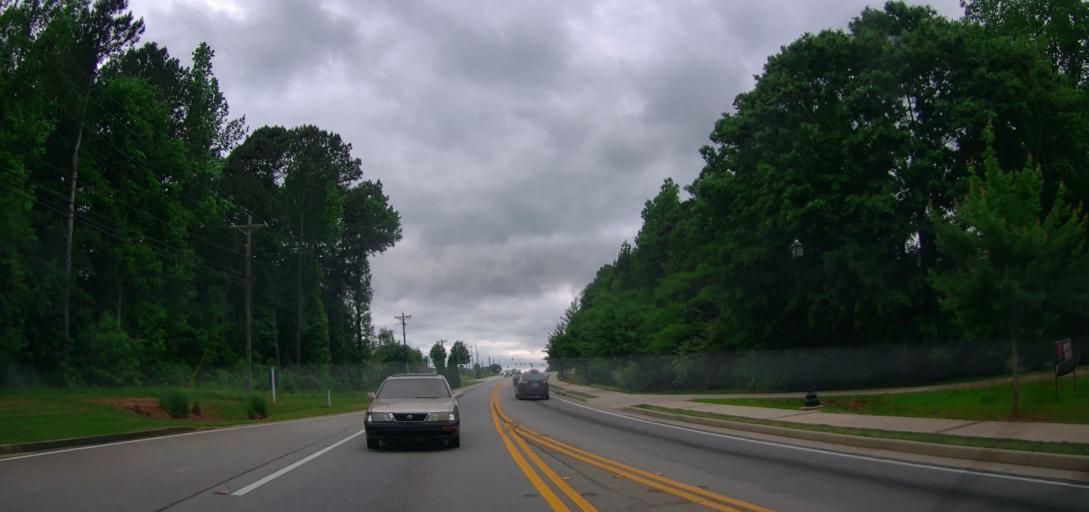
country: US
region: Georgia
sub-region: Walton County
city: Monroe
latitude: 33.7924
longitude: -83.7398
